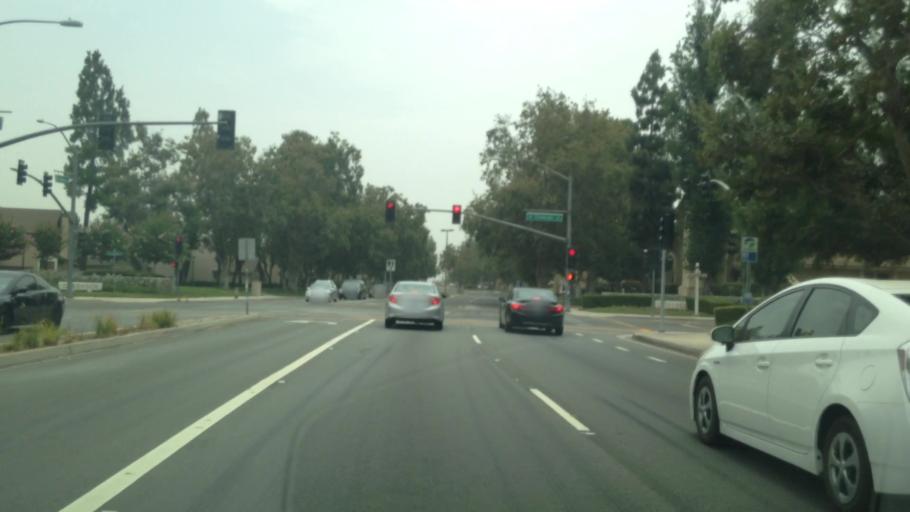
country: US
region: California
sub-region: Riverside County
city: Mira Loma
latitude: 34.0231
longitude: -117.5753
